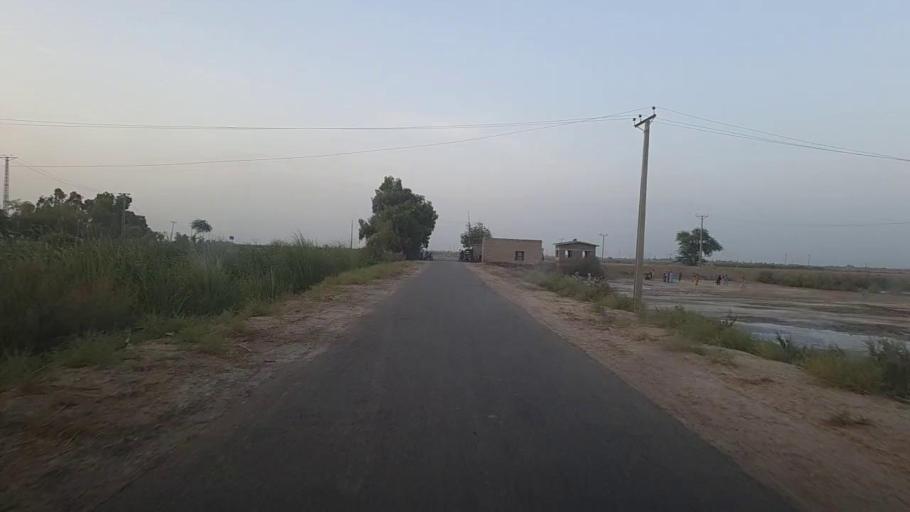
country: PK
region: Sindh
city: Radhan
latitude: 27.1431
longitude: 67.9354
